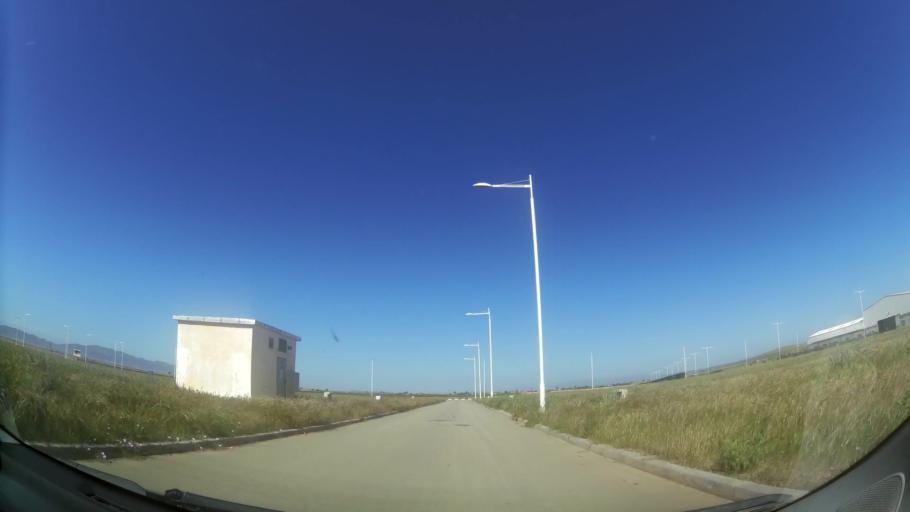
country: MA
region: Oriental
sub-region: Oujda-Angad
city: Oujda
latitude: 34.7724
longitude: -1.9318
